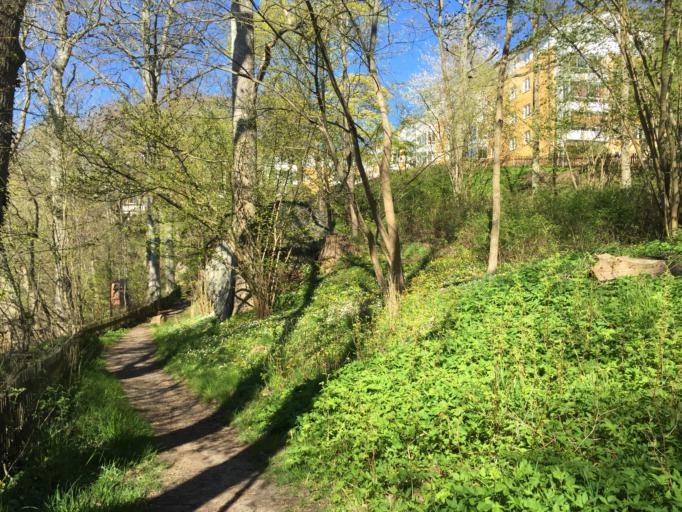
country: SE
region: Blekinge
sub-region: Karlskrona Kommun
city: Rodeby
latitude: 56.1976
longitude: 15.6626
